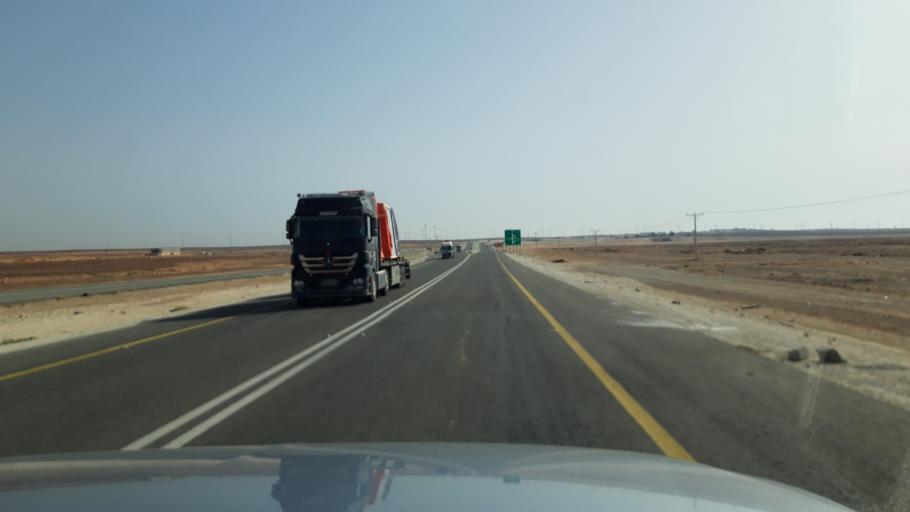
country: JO
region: Amman
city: Al Azraq ash Shamali
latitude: 31.8696
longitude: 36.7251
